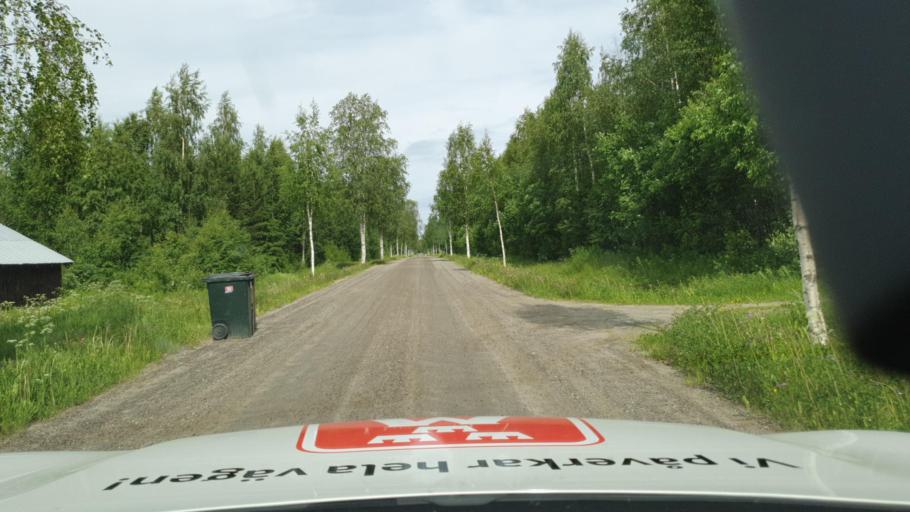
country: SE
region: Vaesterbotten
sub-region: Skelleftea Kommun
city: Burtraesk
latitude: 64.4671
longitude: 20.4697
